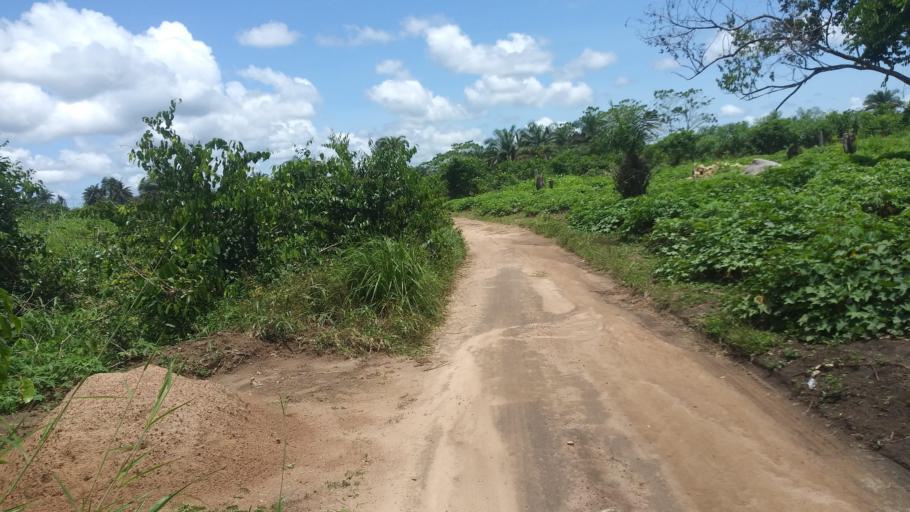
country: SL
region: Northern Province
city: Makeni
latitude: 8.8837
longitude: -12.0177
